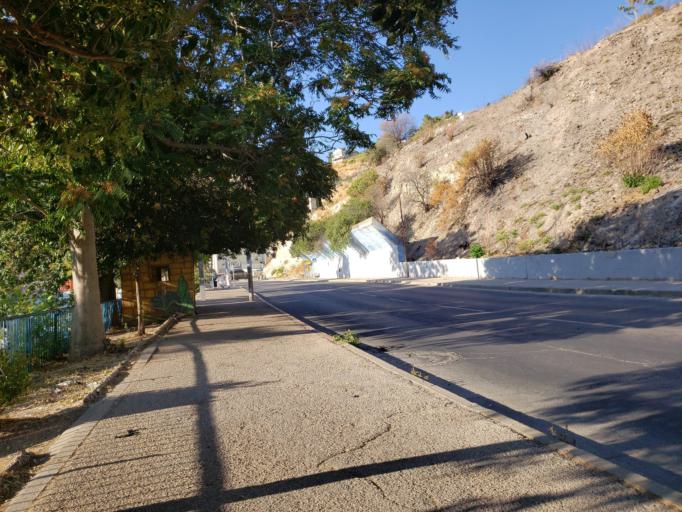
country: IL
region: Northern District
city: Safed
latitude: 32.9629
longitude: 35.4918
